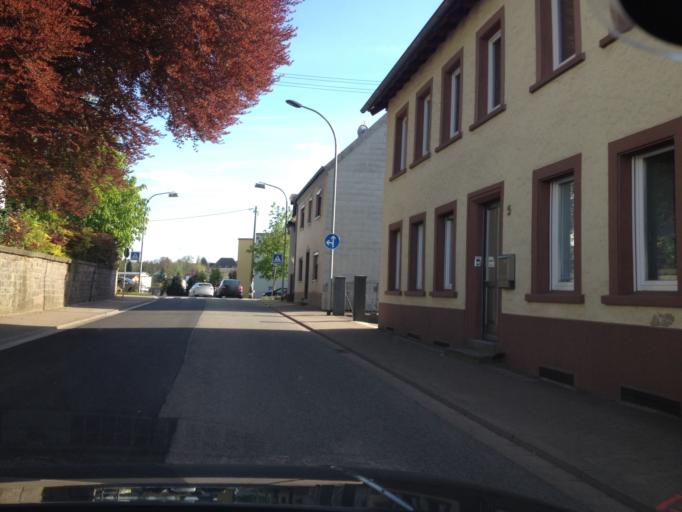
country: DE
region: Saarland
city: Sankt Wendel
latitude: 49.4685
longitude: 7.1759
